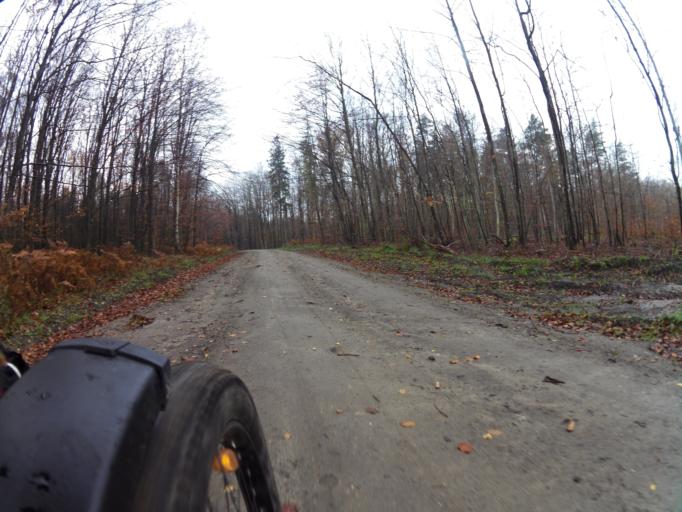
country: PL
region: Pomeranian Voivodeship
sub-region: Powiat pucki
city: Krokowa
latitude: 54.7710
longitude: 18.0928
